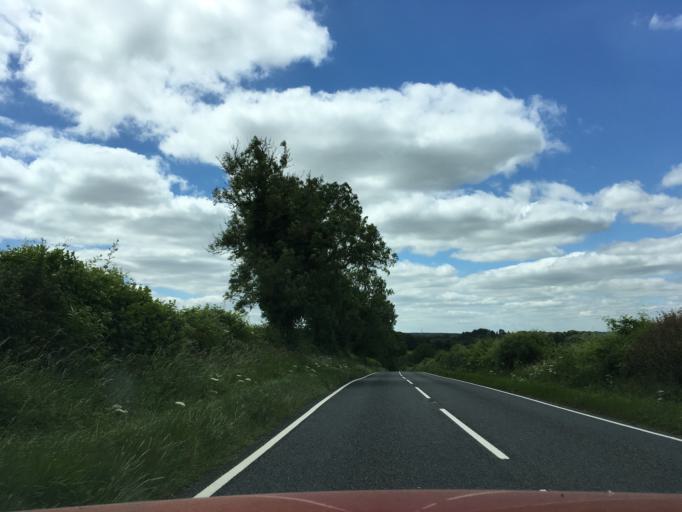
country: GB
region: England
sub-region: Hampshire
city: Highclere
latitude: 51.3002
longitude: -1.4052
